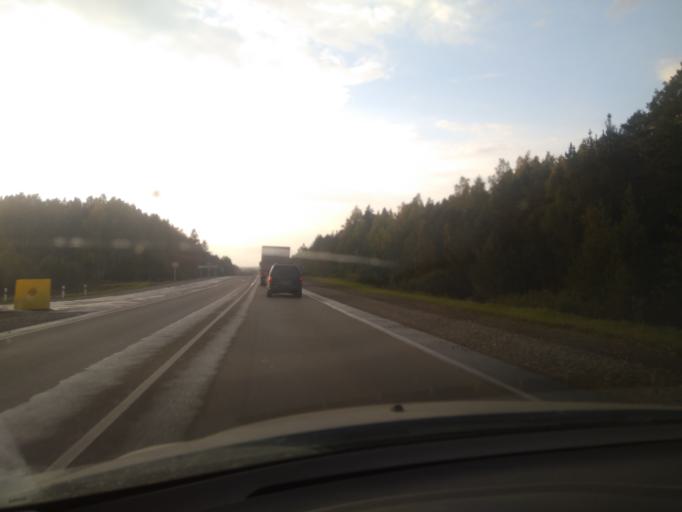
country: RU
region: Sverdlovsk
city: Verkhneye Dubrovo
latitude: 56.7247
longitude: 61.0424
